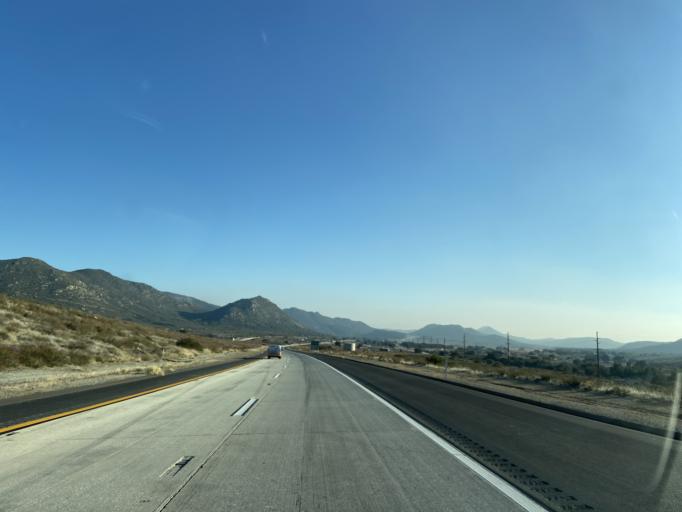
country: US
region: California
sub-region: San Diego County
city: Pine Valley
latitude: 32.7724
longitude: -116.4916
